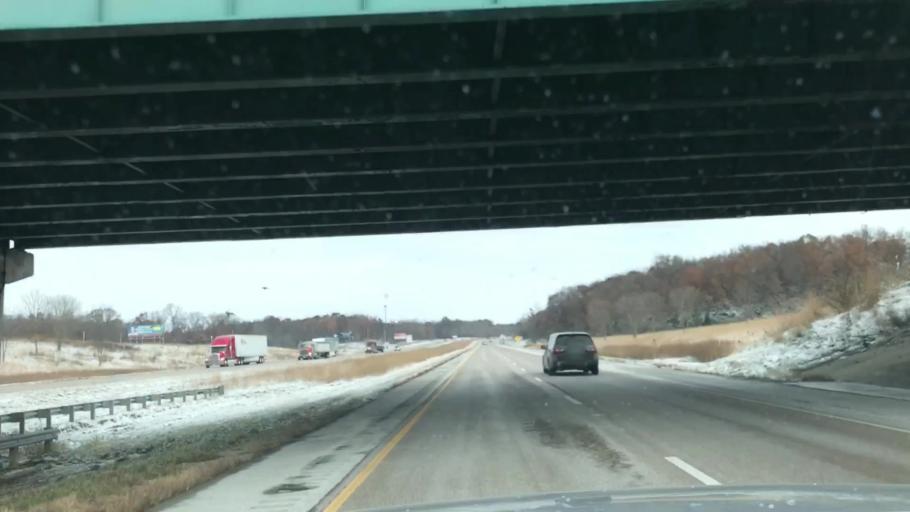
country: US
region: Illinois
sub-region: Macoupin County
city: Mount Olive
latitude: 39.0720
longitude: -89.7556
